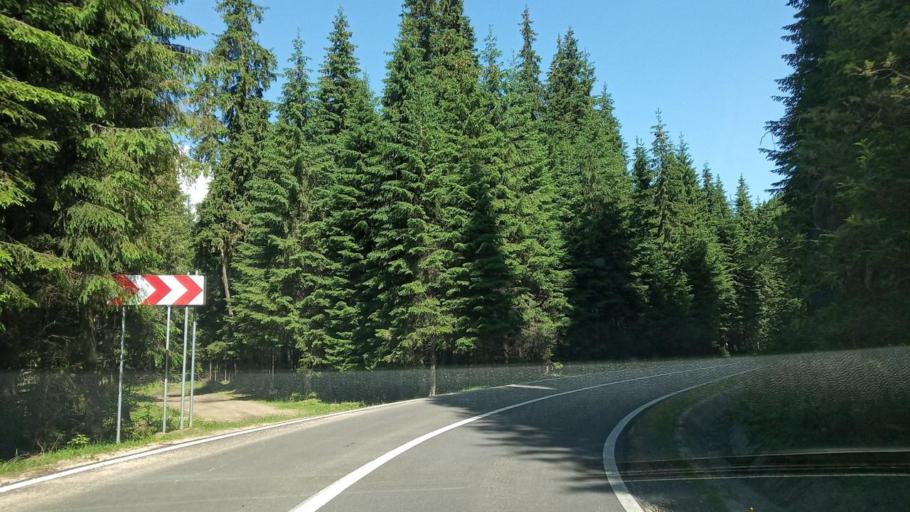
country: RO
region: Alba
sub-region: Comuna Sugag
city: Sugag
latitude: 45.5310
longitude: 23.6439
